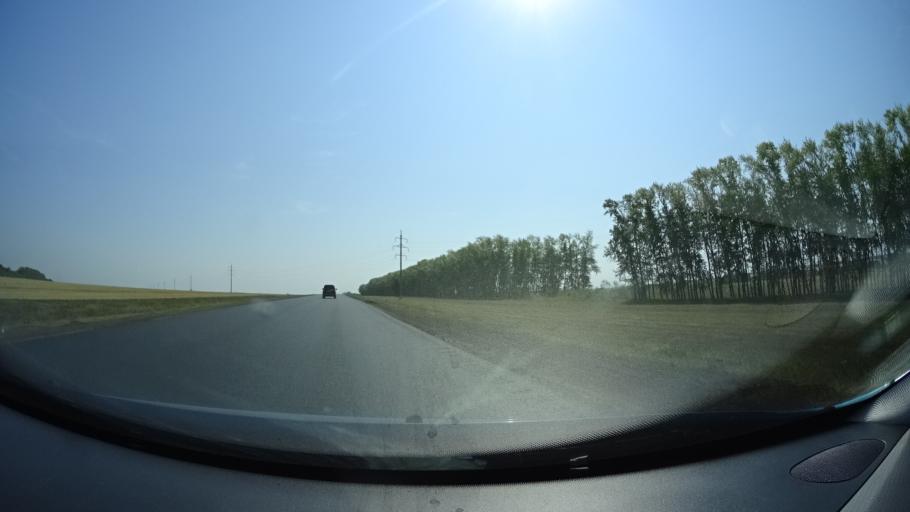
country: RU
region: Bashkortostan
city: Kabakovo
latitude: 54.4349
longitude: 56.0110
